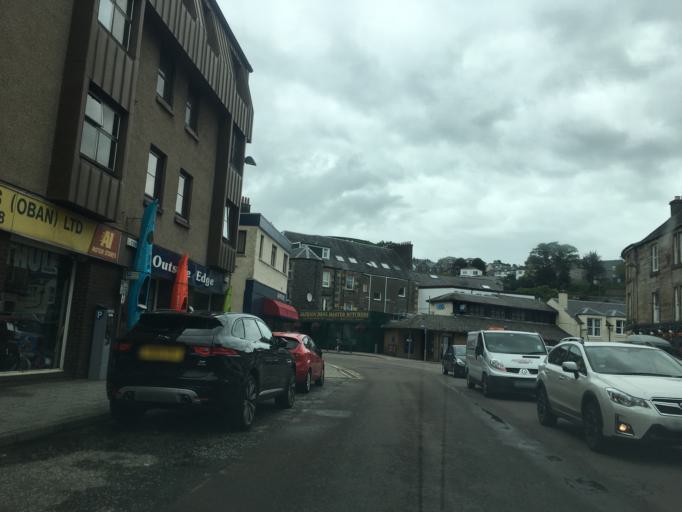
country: GB
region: Scotland
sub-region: Argyll and Bute
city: Oban
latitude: 56.4125
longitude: -5.4724
